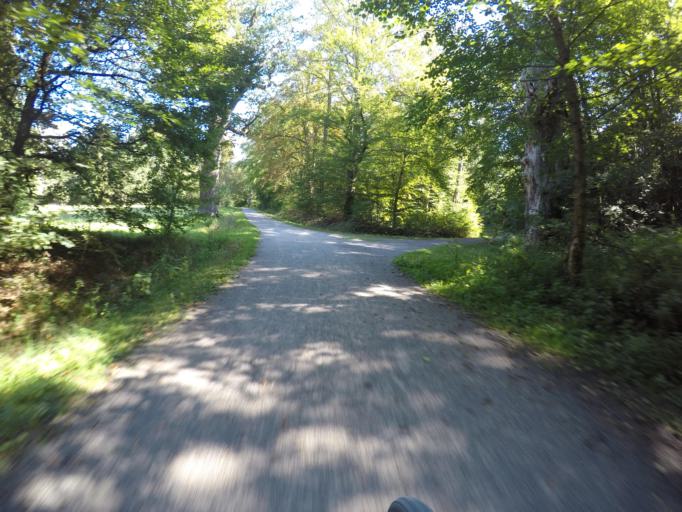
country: DE
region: Baden-Wuerttemberg
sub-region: Regierungsbezirk Stuttgart
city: Gerlingen
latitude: 48.7621
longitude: 9.0952
